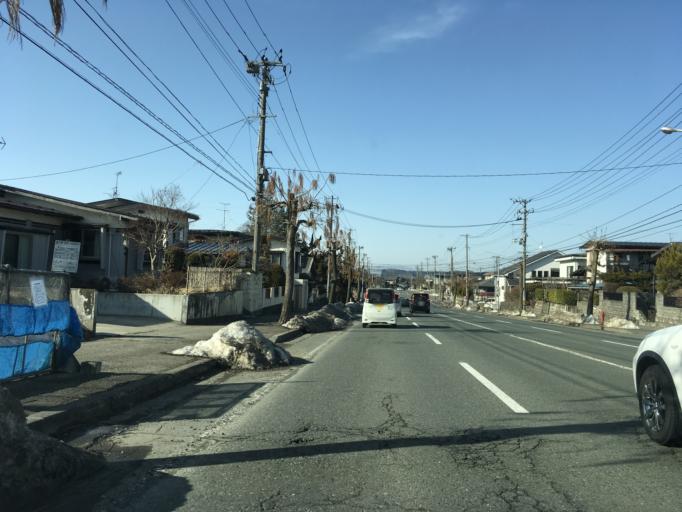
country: JP
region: Iwate
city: Morioka-shi
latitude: 39.7463
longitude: 141.1678
